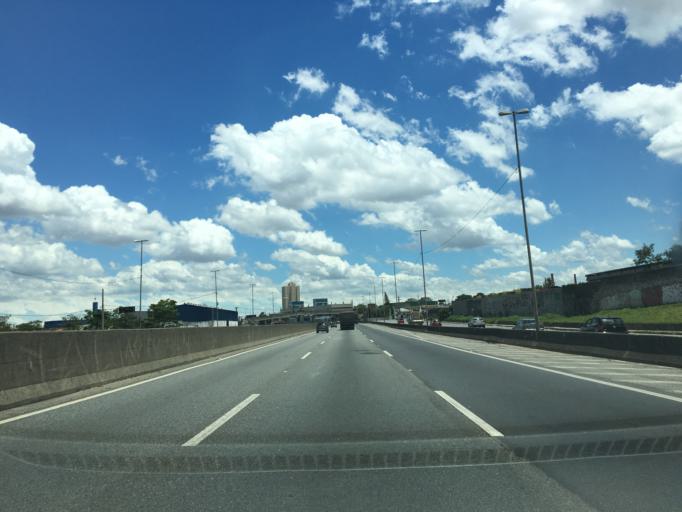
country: BR
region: Sao Paulo
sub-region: Guarulhos
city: Guarulhos
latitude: -23.4638
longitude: -46.5716
